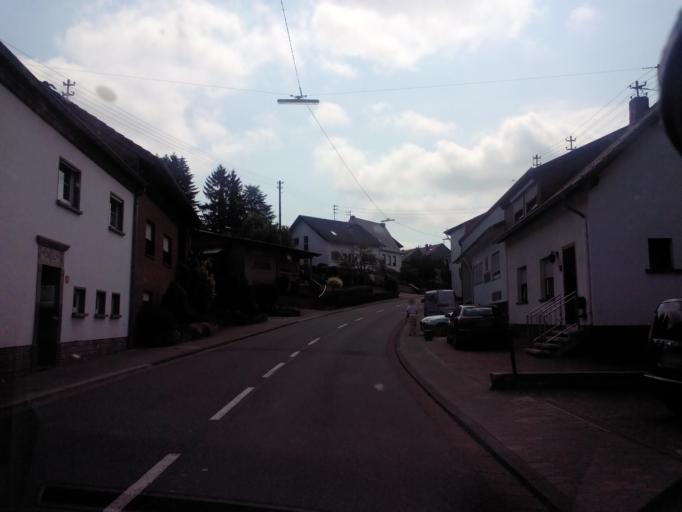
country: DE
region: Saarland
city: Eppelborn
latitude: 49.4047
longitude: 6.9688
